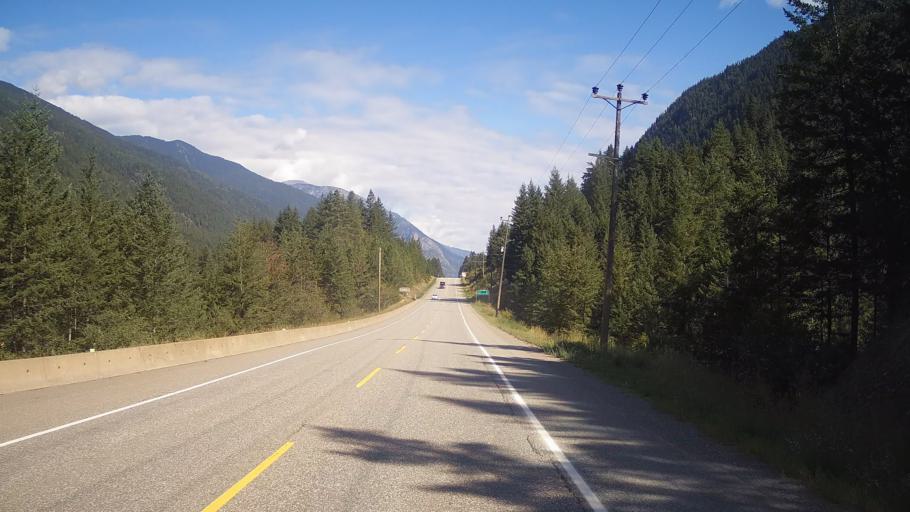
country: CA
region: British Columbia
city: Hope
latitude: 50.0307
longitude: -121.5300
